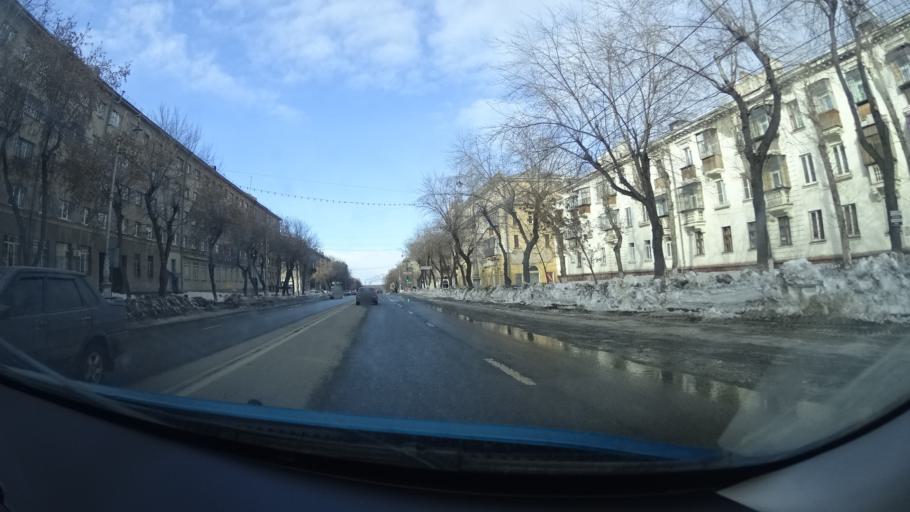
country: RU
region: Chelyabinsk
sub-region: Gorod Magnitogorsk
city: Magnitogorsk
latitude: 53.4308
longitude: 58.9837
